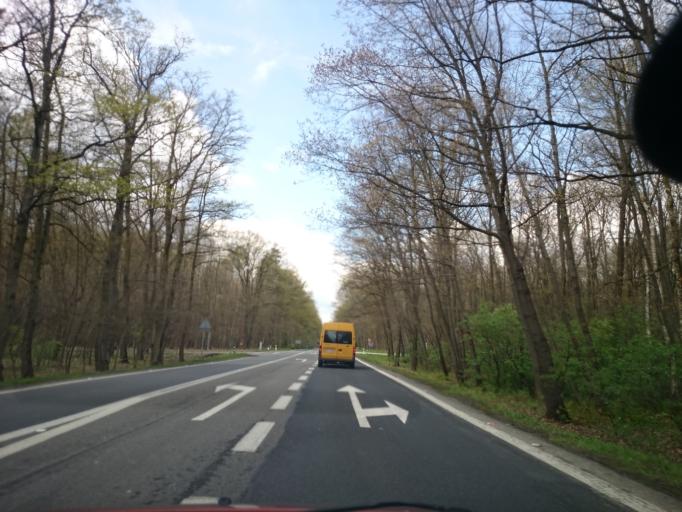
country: PL
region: Opole Voivodeship
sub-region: Powiat opolski
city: Tarnow Opolski
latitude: 50.5947
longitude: 18.0930
